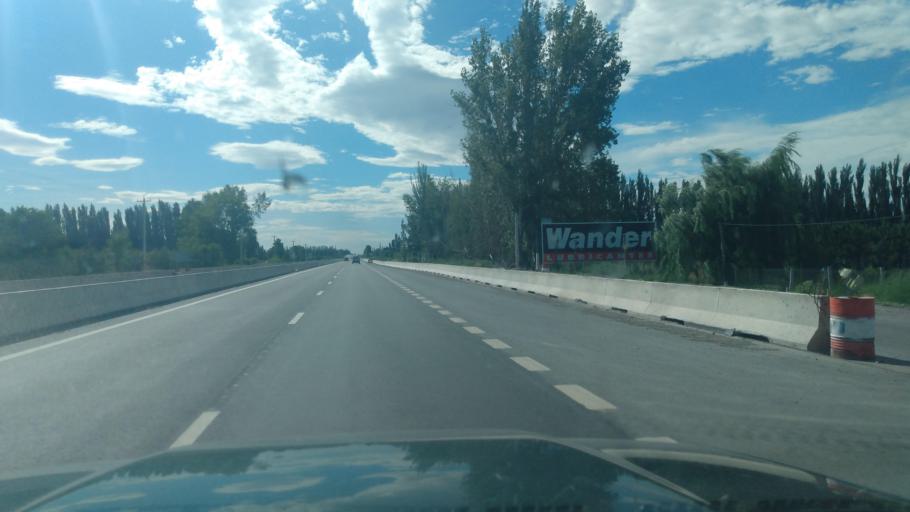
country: AR
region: Rio Negro
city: General Fernandez Oro
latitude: -38.9858
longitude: -67.9230
